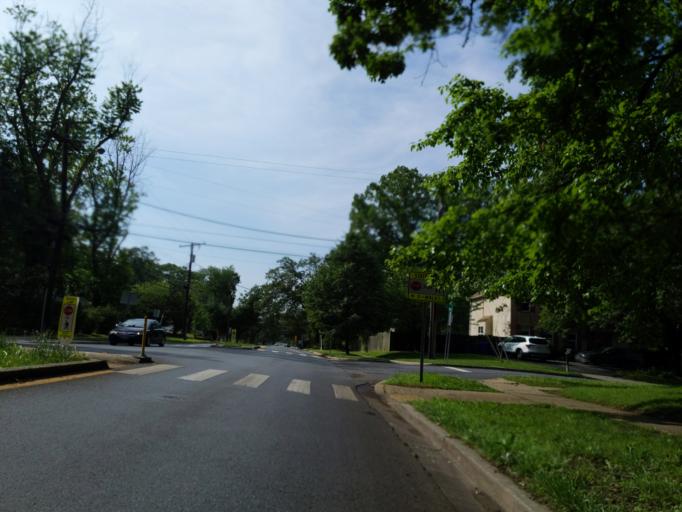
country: US
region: Maryland
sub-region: Montgomery County
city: Kemp Mill
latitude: 39.0439
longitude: -77.0307
